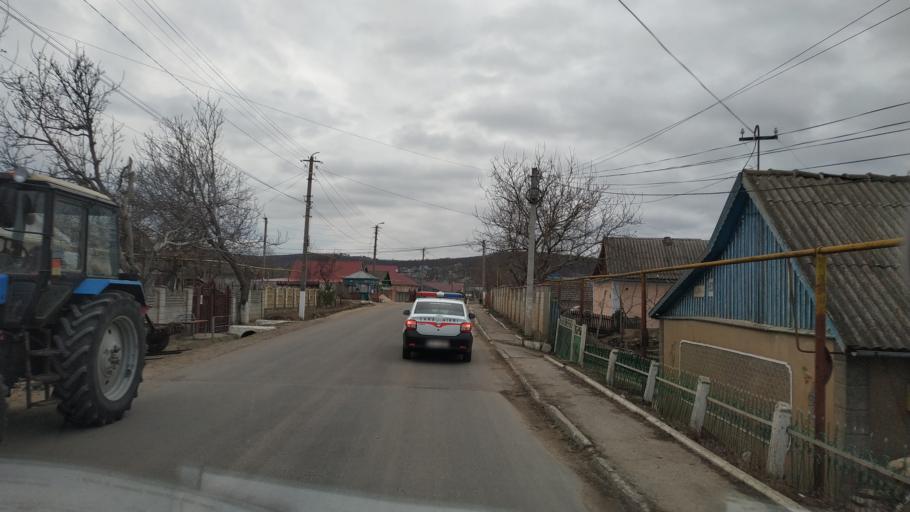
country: MD
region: Causeni
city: Causeni
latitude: 46.6523
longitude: 29.4434
